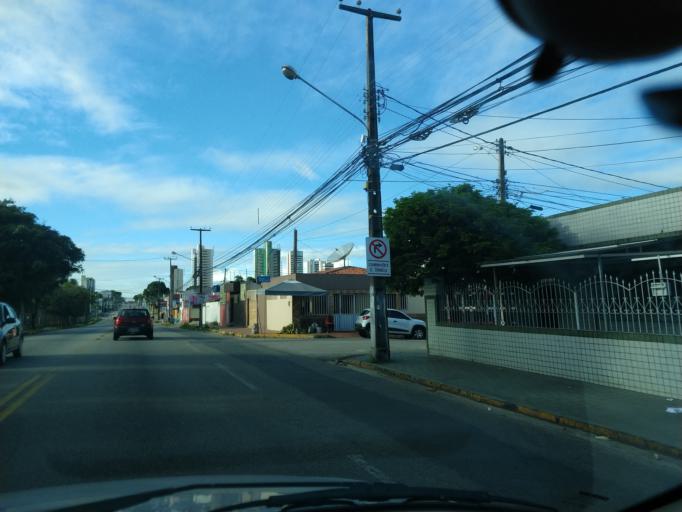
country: BR
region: Rio Grande do Norte
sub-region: Natal
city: Natal
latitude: -5.8253
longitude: -35.2206
